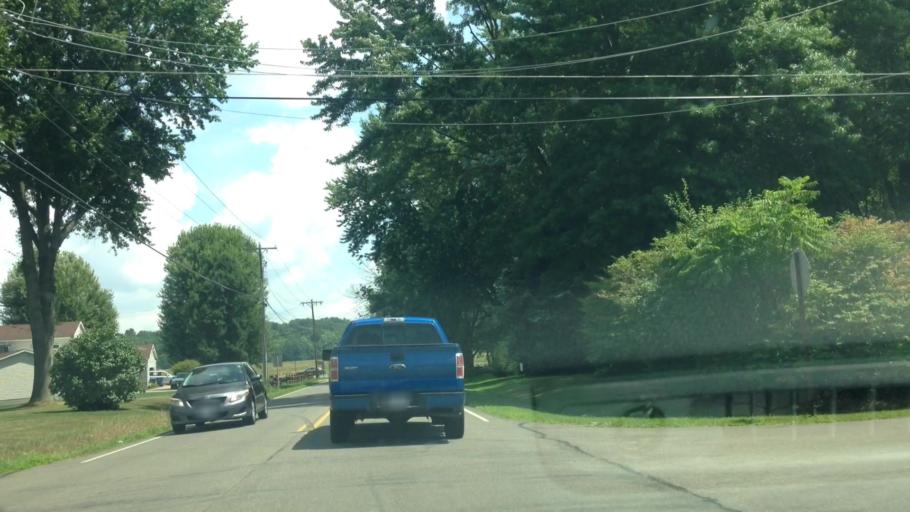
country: US
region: Ohio
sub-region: Summit County
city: New Franklin
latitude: 40.9490
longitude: -81.5357
